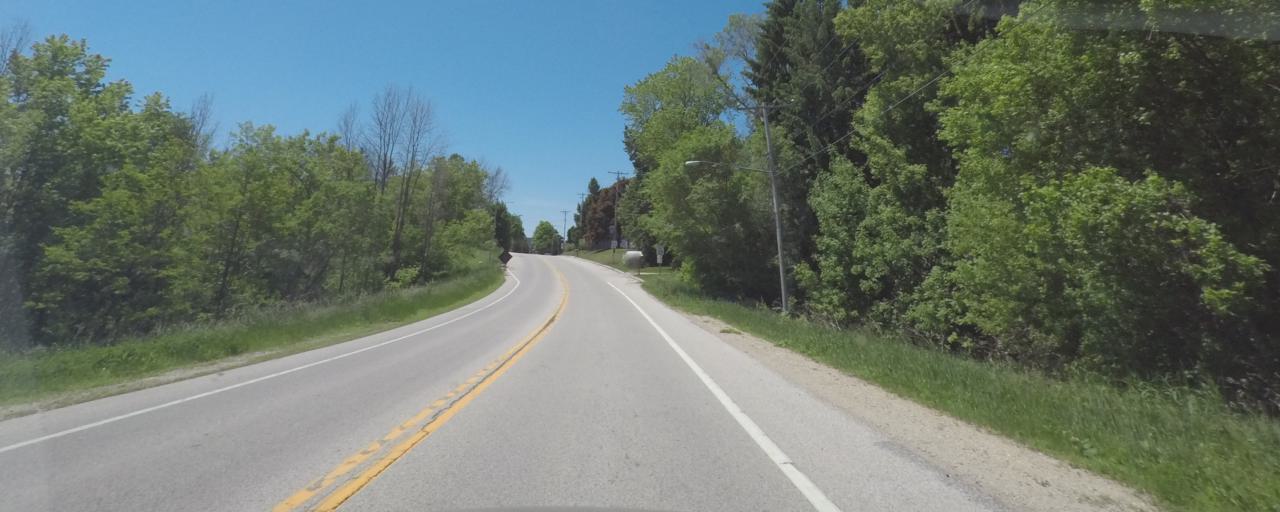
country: US
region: Wisconsin
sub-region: Sheboygan County
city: Plymouth
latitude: 43.6608
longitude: -88.0022
